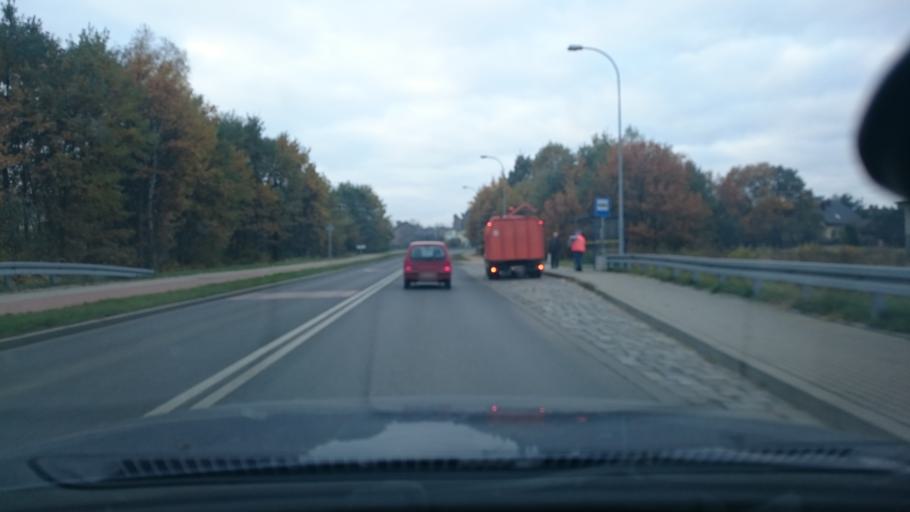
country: PL
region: Silesian Voivodeship
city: Zebrzydowice
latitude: 50.1188
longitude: 18.5185
